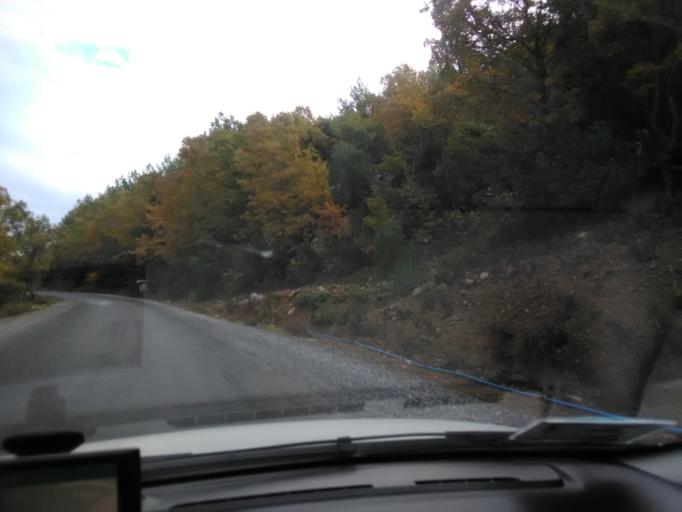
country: TR
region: Antalya
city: Gazipasa
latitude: 36.2466
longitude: 32.4405
